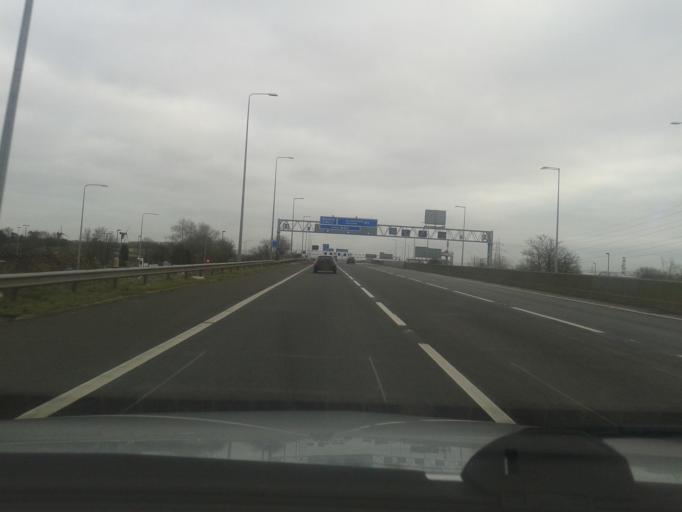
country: GB
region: England
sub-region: South Gloucestershire
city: Almondsbury
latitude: 51.5466
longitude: -2.5702
